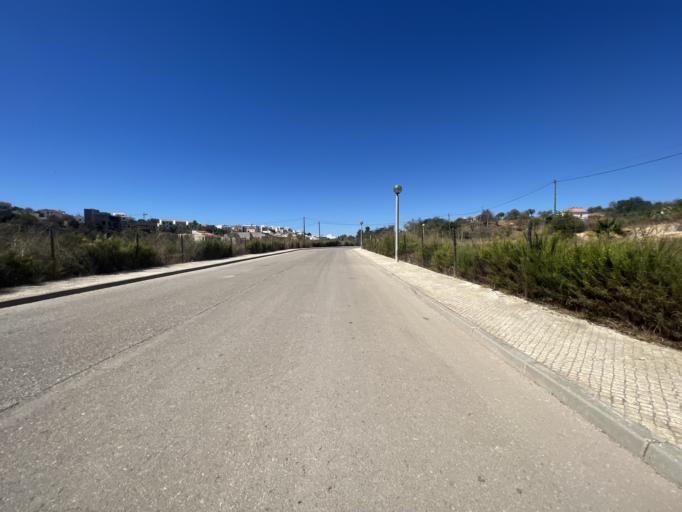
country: PT
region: Faro
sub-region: Portimao
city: Portimao
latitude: 37.1258
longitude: -8.5127
